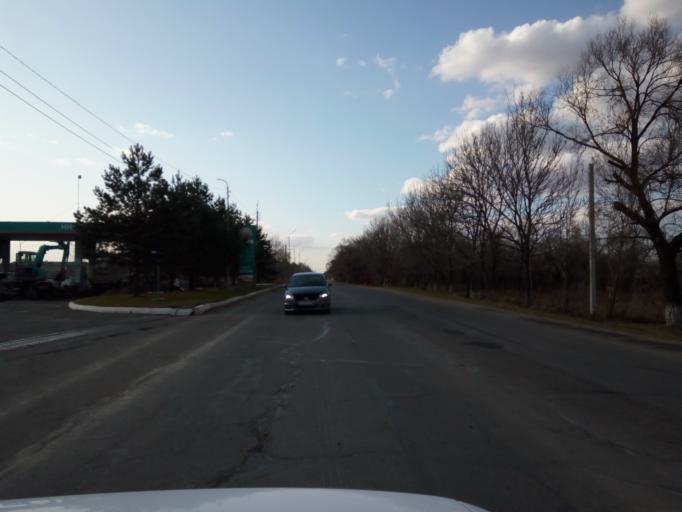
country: RU
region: Primorskiy
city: Dal'nerechensk
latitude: 45.9176
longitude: 133.7625
